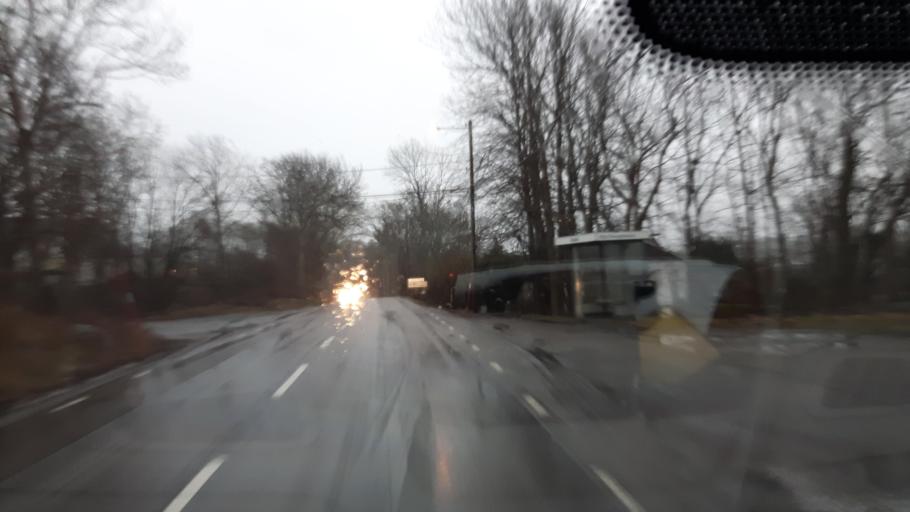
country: SE
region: Halland
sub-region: Kungsbacka Kommun
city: Onsala
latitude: 57.3974
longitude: 11.9954
